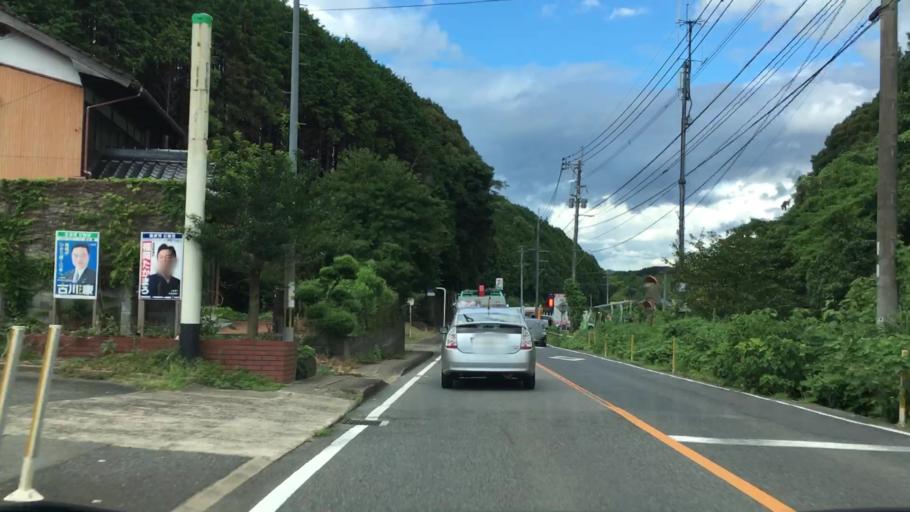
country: JP
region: Saga Prefecture
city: Imaricho-ko
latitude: 33.2916
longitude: 129.9089
